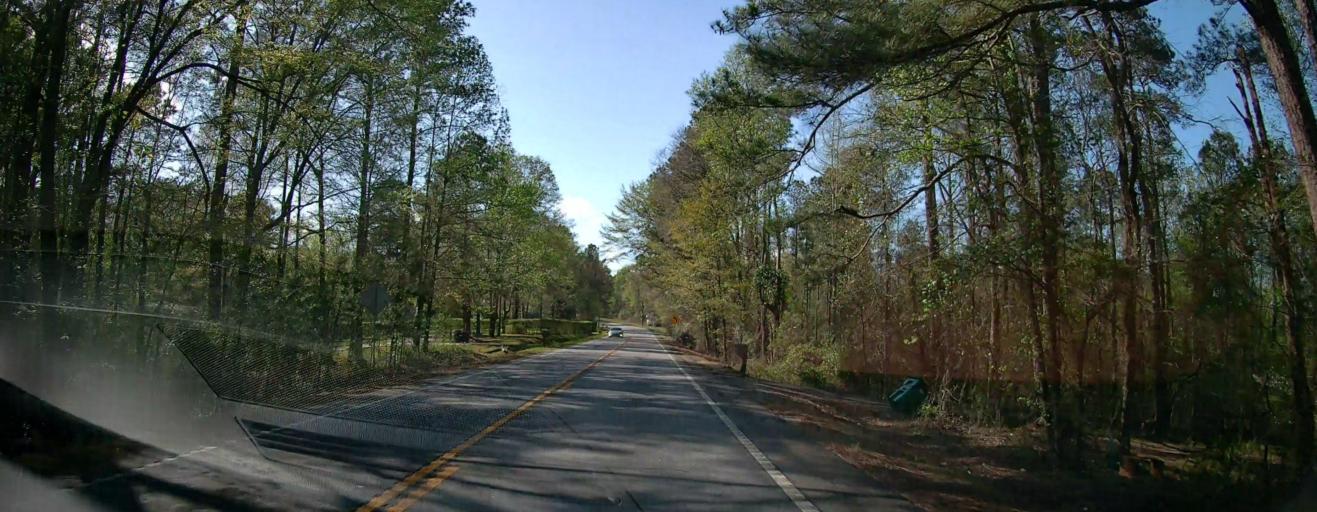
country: US
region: Georgia
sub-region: Baldwin County
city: Hardwick
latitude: 33.0894
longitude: -83.1752
